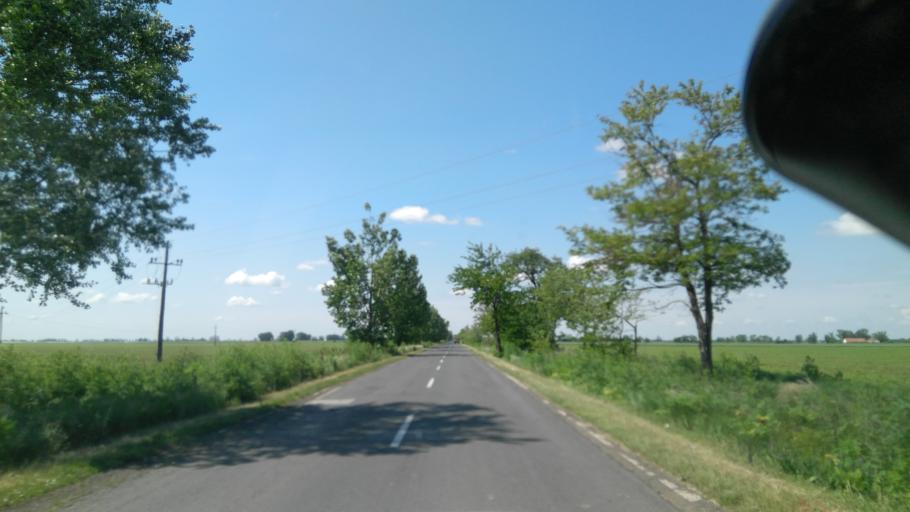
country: HU
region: Bekes
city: Medgyesegyhaza
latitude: 46.4701
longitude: 21.0155
